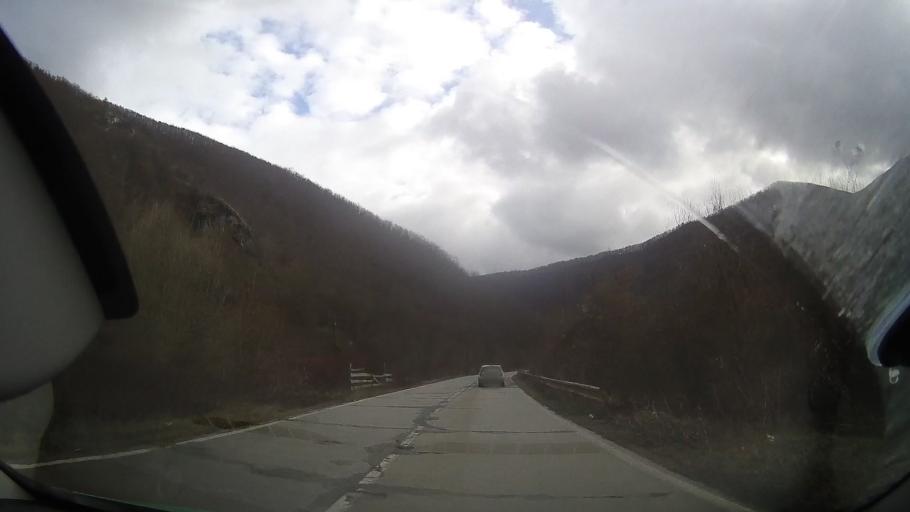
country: RO
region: Alba
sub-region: Comuna Rimetea
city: Rimetea
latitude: 46.5085
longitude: 23.5696
